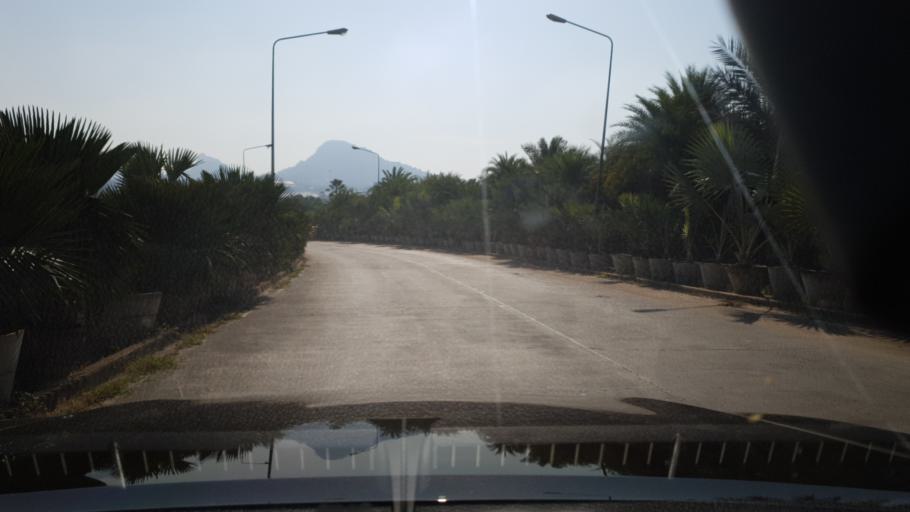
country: TH
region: Chon Buri
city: Sattahip
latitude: 12.7758
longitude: 100.9213
